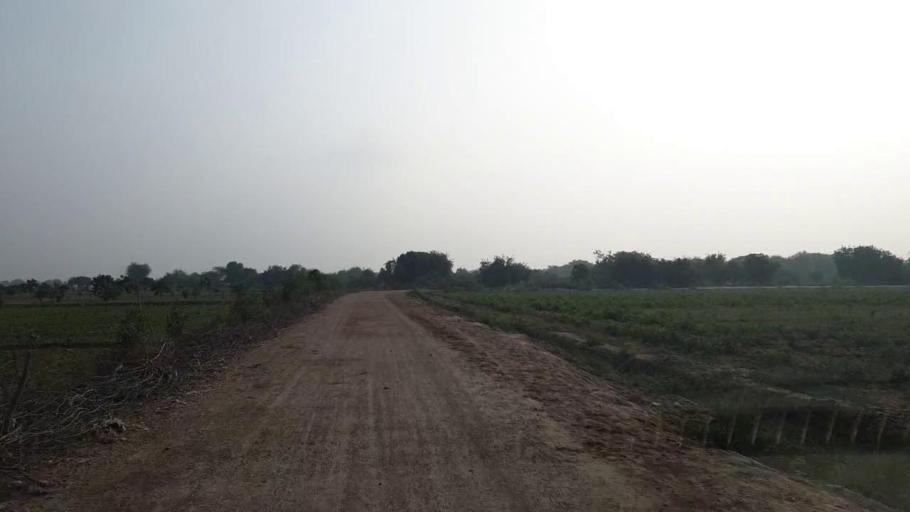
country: PK
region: Sindh
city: Tando Muhammad Khan
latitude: 25.1615
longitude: 68.5946
